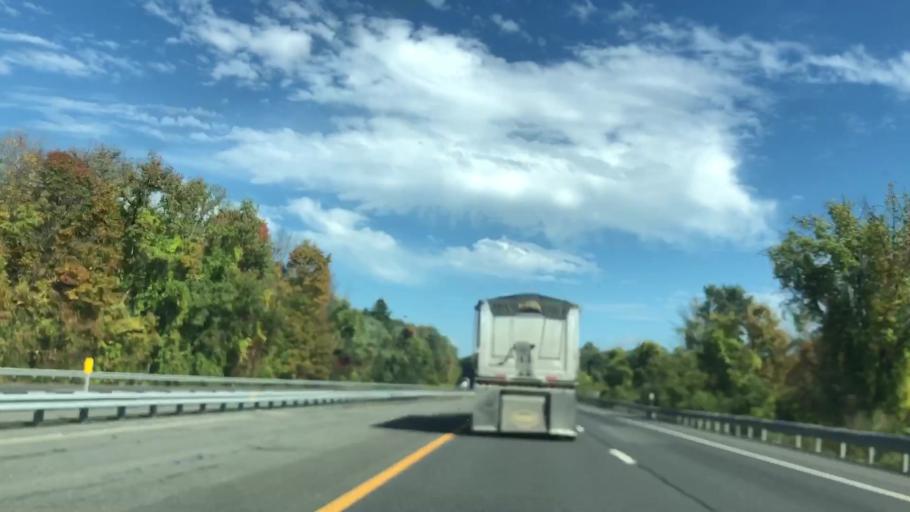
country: US
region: New York
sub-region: Ulster County
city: Rosendale Village
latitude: 41.8581
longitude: -74.0579
